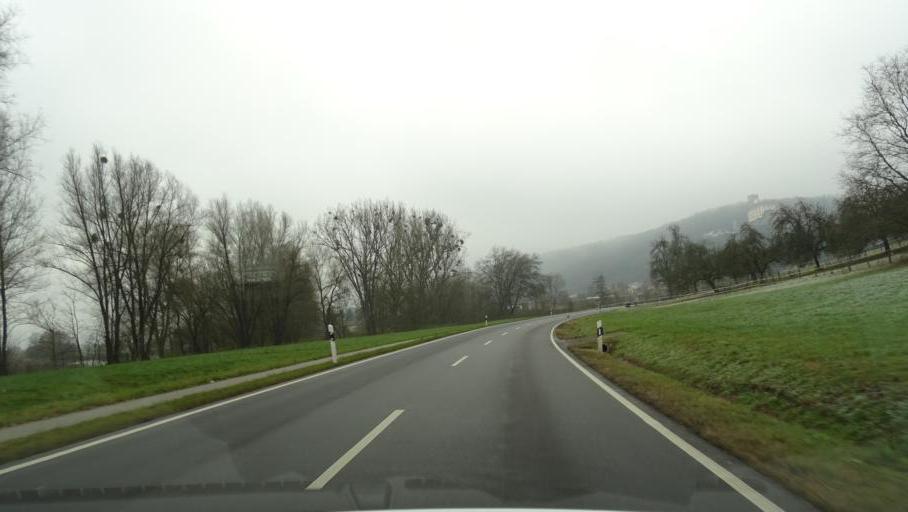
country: DE
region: Baden-Wuerttemberg
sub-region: Karlsruhe Region
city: Hassmersheim
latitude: 49.2880
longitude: 9.1319
